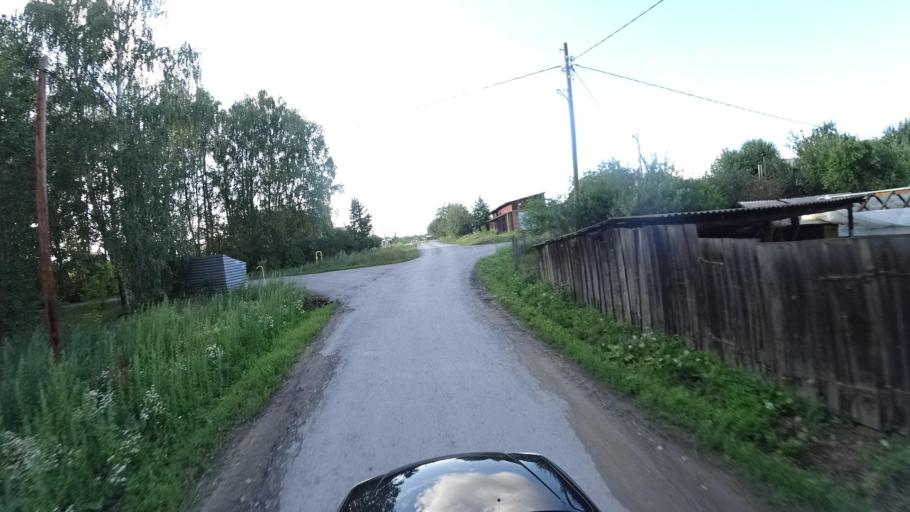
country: RU
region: Sverdlovsk
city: Obukhovskoye
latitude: 56.8489
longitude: 62.6535
